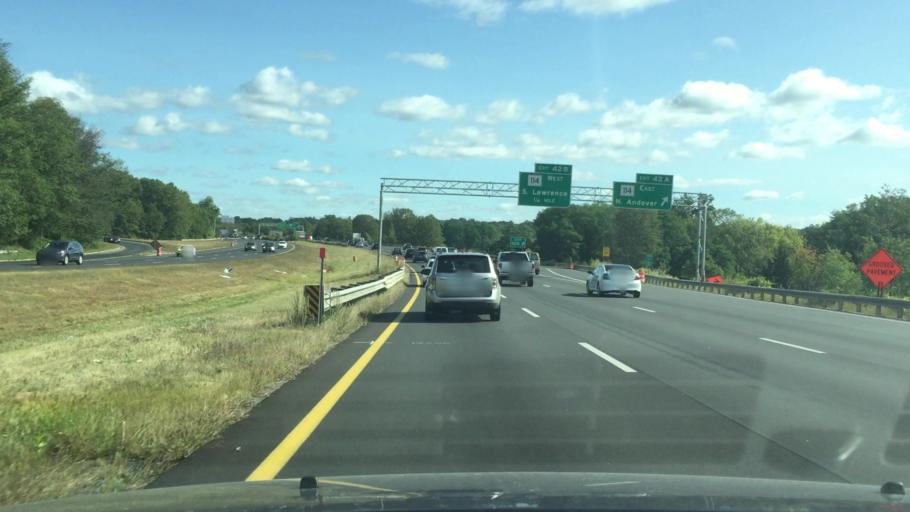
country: US
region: Massachusetts
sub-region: Essex County
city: North Andover
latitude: 42.6829
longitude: -71.1453
